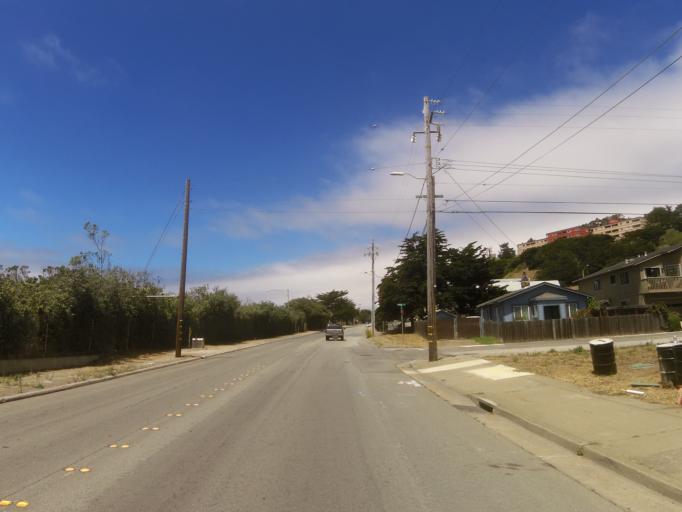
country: US
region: California
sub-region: San Mateo County
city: Pacifica
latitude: 37.6318
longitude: -122.4892
